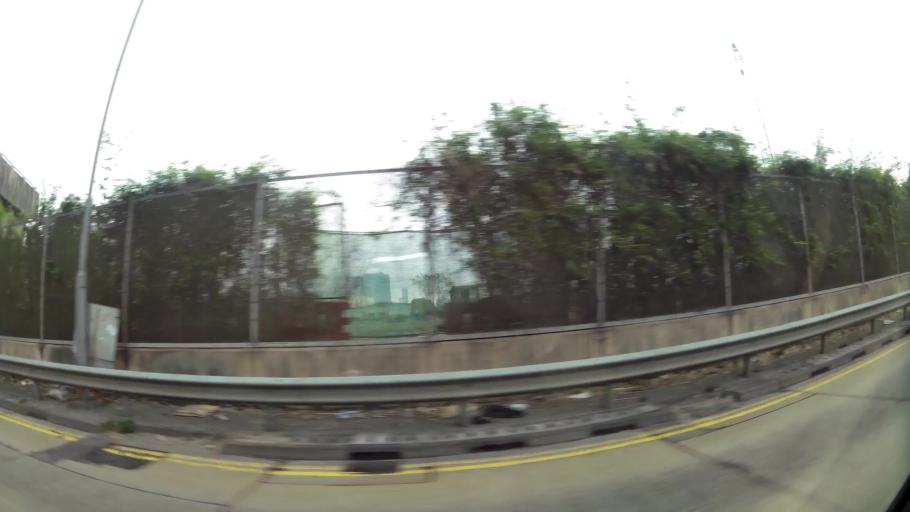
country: HK
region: Kowloon City
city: Kowloon
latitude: 22.3302
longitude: 114.1943
